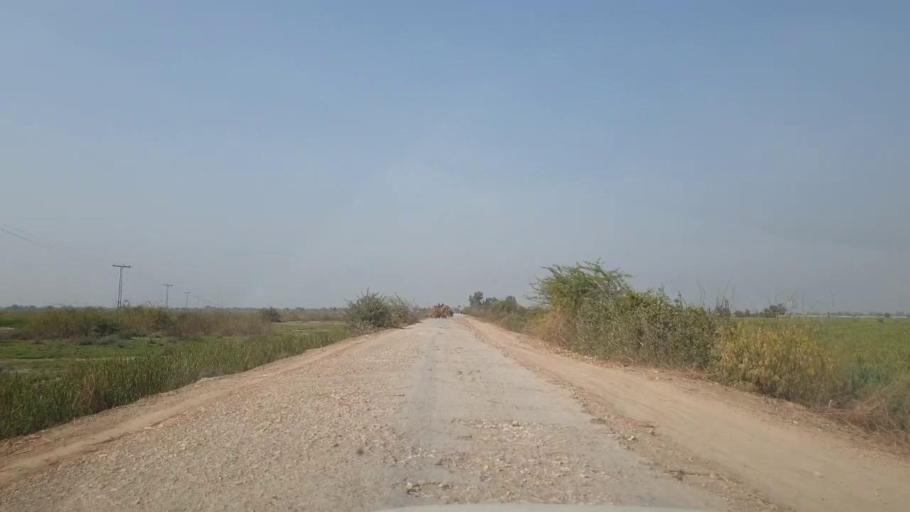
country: PK
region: Sindh
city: Mirpur Khas
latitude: 25.6945
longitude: 69.1480
